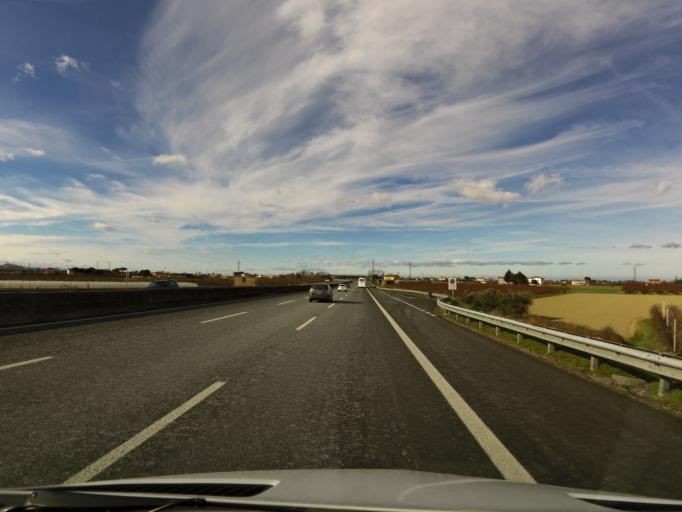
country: IT
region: Emilia-Romagna
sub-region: Forli-Cesena
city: Bagnarola
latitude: 44.1552
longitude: 12.3150
